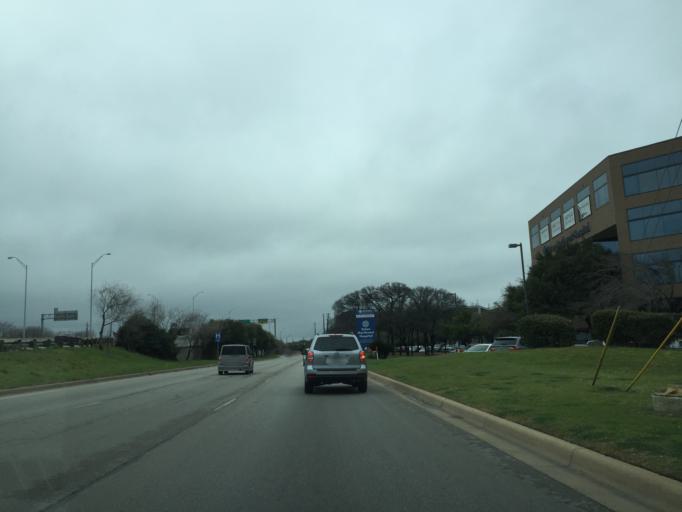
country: US
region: Texas
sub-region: Williamson County
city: Jollyville
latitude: 30.4049
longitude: -97.7450
